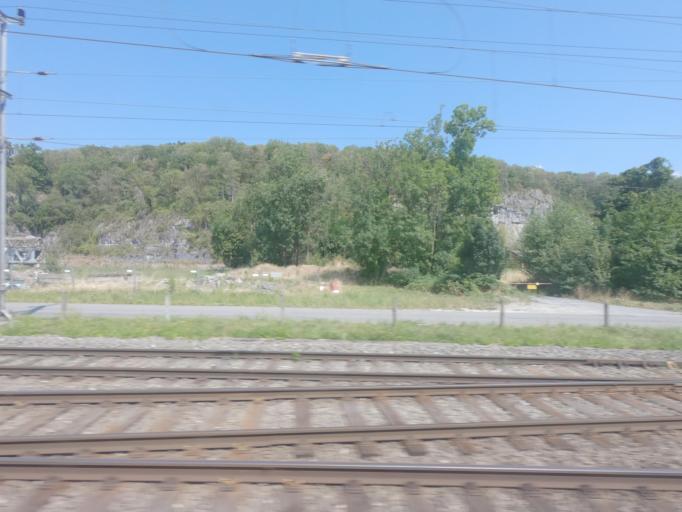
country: CH
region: Vaud
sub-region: Aigle District
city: Ollon
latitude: 46.2856
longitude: 6.9702
